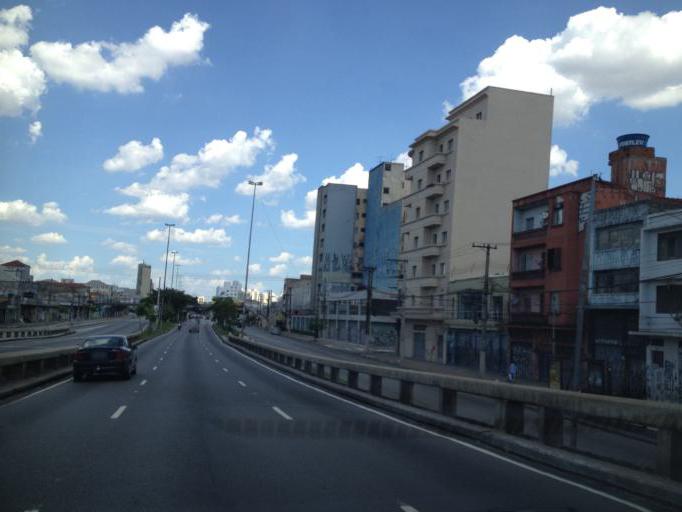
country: BR
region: Sao Paulo
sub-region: Sao Paulo
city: Sao Paulo
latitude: -23.5519
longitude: -46.6243
